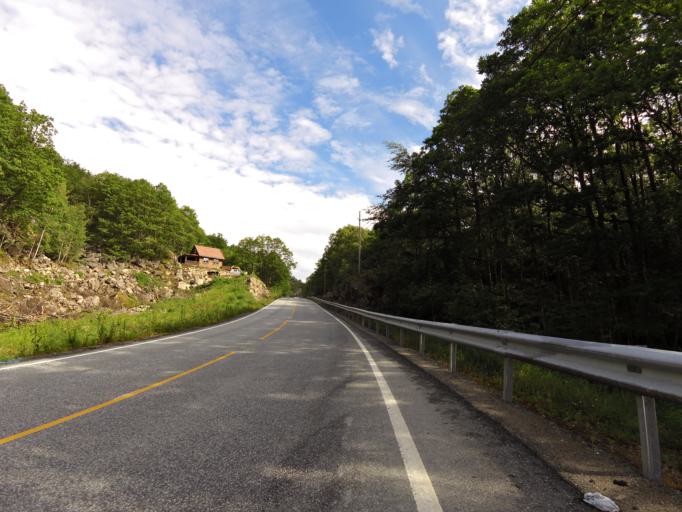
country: NO
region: Vest-Agder
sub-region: Lindesnes
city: Vigeland
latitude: 58.0504
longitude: 7.1755
